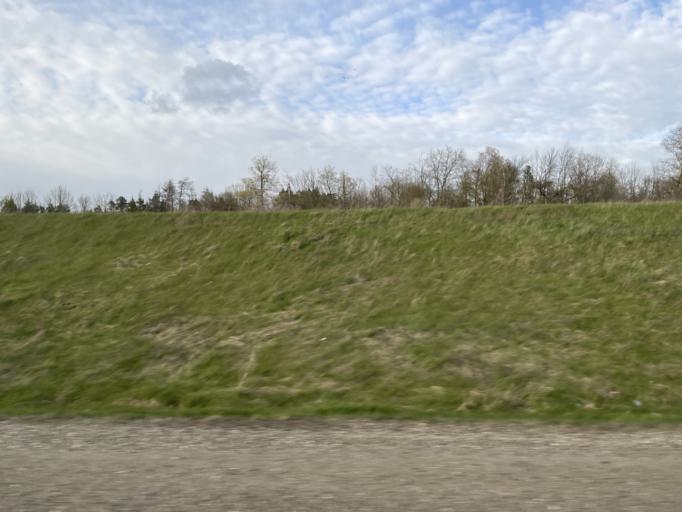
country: CA
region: Ontario
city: Waterloo
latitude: 43.4803
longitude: -80.4070
